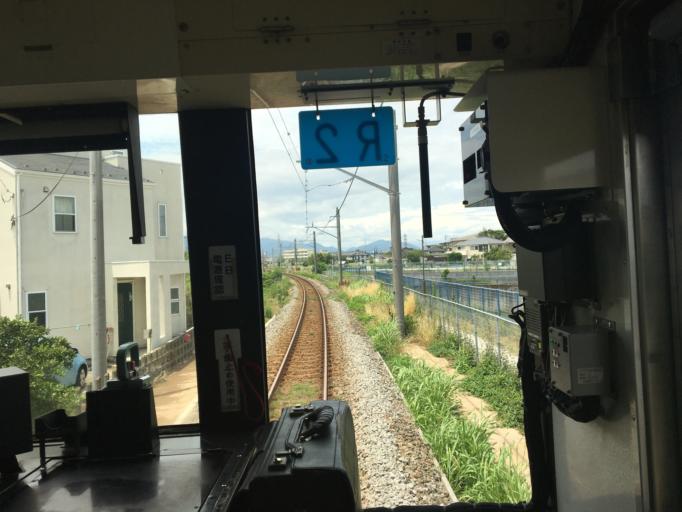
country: JP
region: Kanagawa
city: Chigasaki
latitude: 35.3602
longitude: 139.3978
